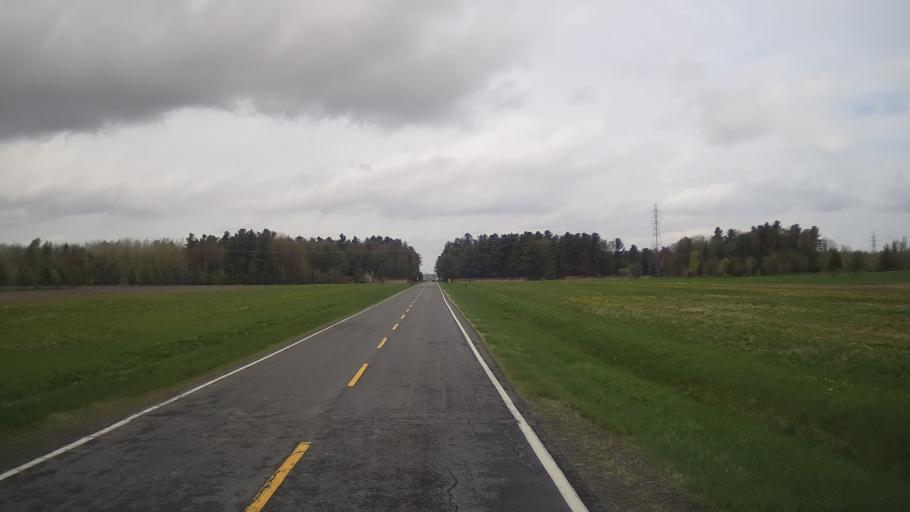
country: CA
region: Quebec
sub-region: Monteregie
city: Marieville
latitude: 45.3110
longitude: -73.1226
